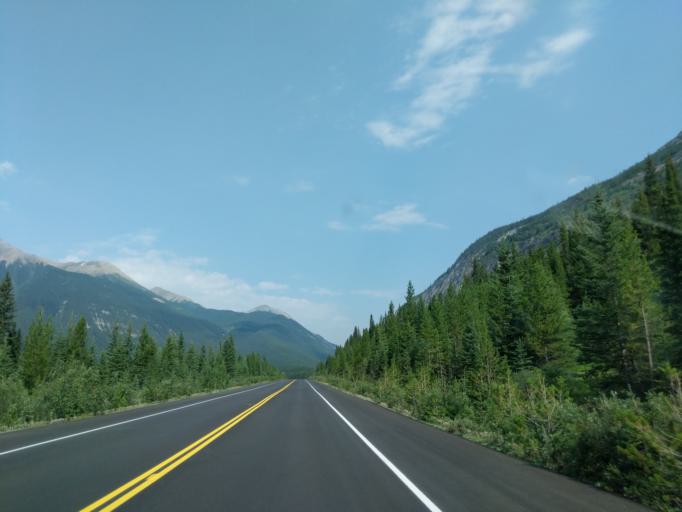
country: CA
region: British Columbia
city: Golden
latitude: 52.1024
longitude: -116.9604
